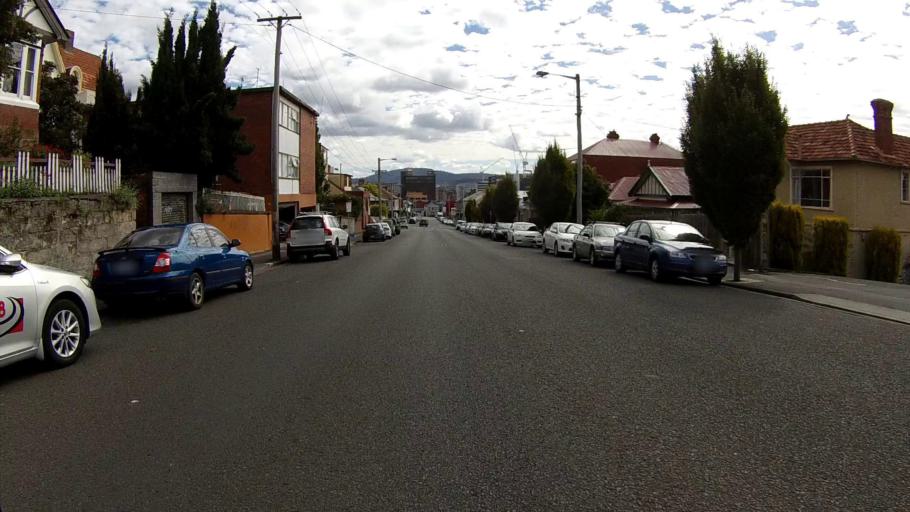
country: AU
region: Tasmania
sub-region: Hobart
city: Sandy Bay
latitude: -42.8858
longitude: 147.3206
